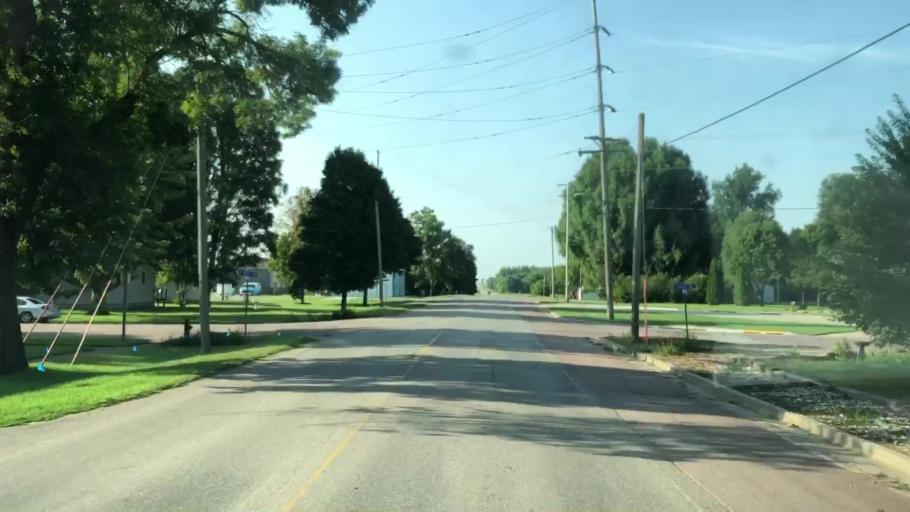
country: US
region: Iowa
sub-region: Lyon County
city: George
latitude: 43.3407
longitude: -95.9985
